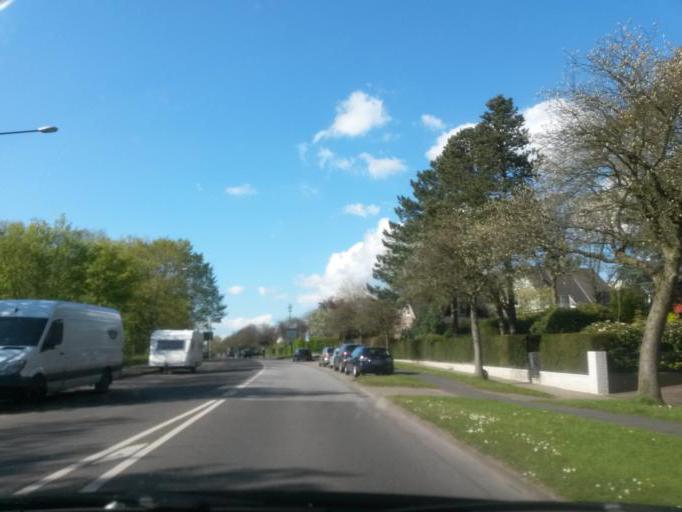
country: DE
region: Schleswig-Holstein
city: Wedel
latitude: 53.5759
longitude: 9.6990
